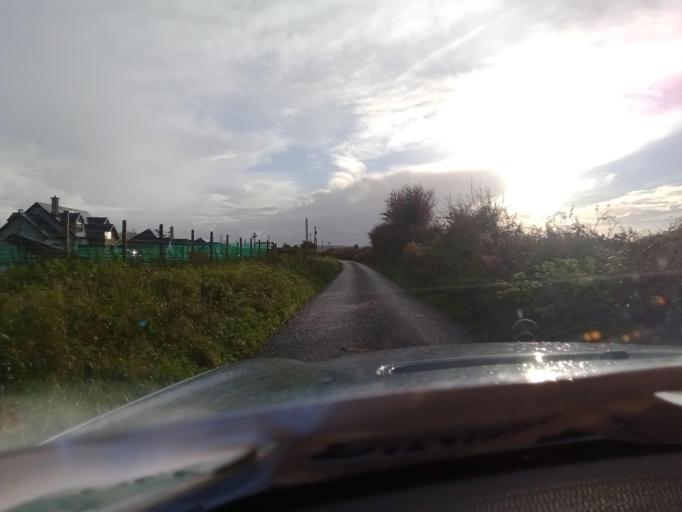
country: IE
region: Leinster
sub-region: Kilkenny
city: Mooncoin
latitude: 52.2789
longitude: -7.1907
